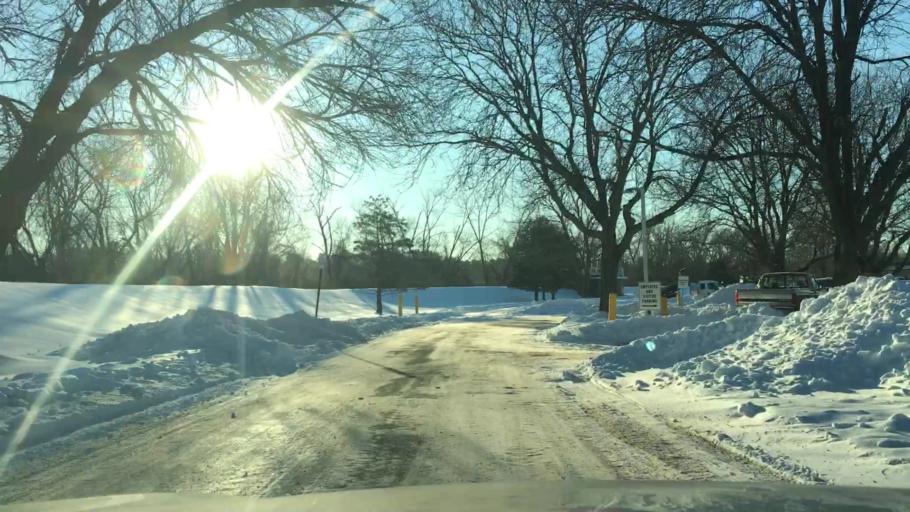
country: US
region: Massachusetts
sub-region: Hampden County
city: Springfield
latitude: 42.0895
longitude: -72.5881
